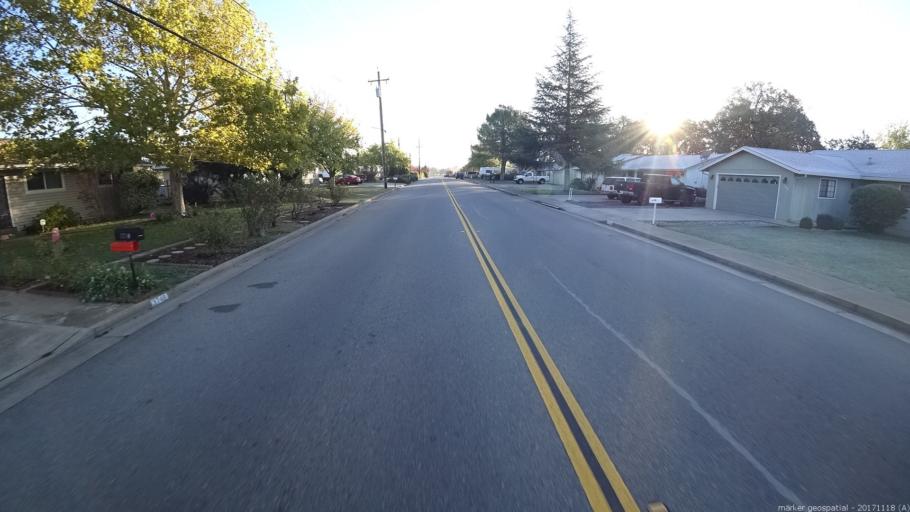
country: US
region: California
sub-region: Shasta County
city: Cottonwood
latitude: 40.3978
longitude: -122.2885
